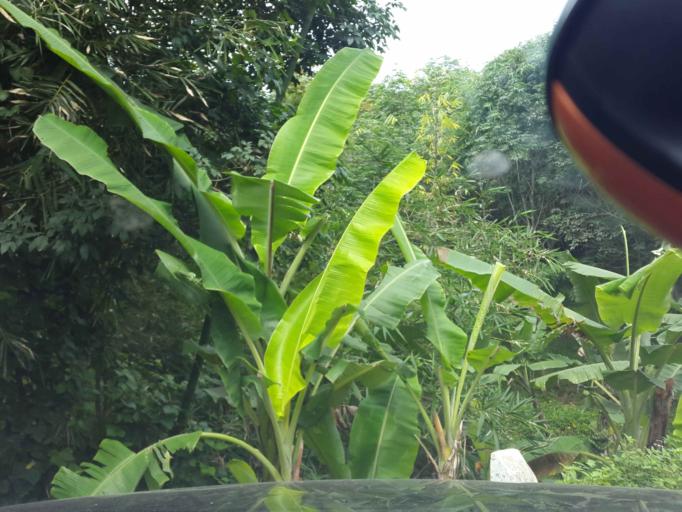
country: ID
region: Central Java
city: Salatiga
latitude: -7.2903
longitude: 110.4939
